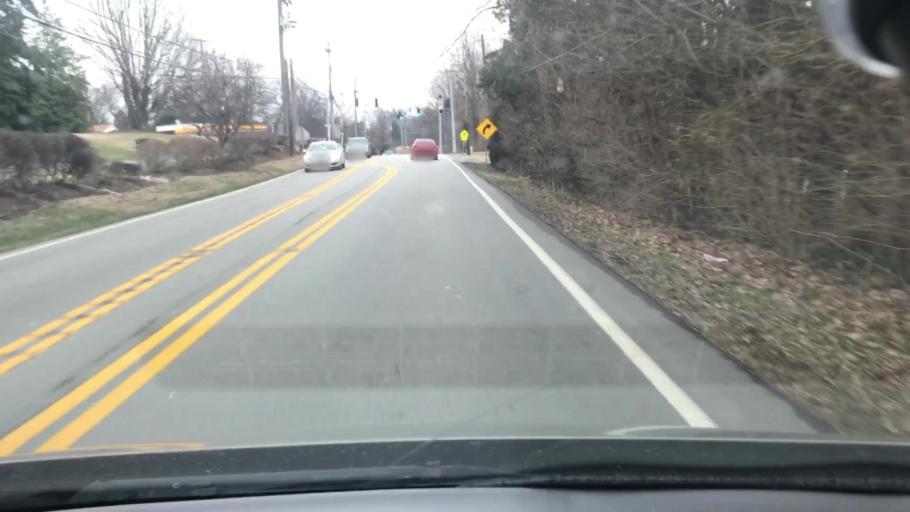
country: US
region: Kentucky
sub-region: Jefferson County
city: Barbourmeade
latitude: 38.2948
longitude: -85.6030
